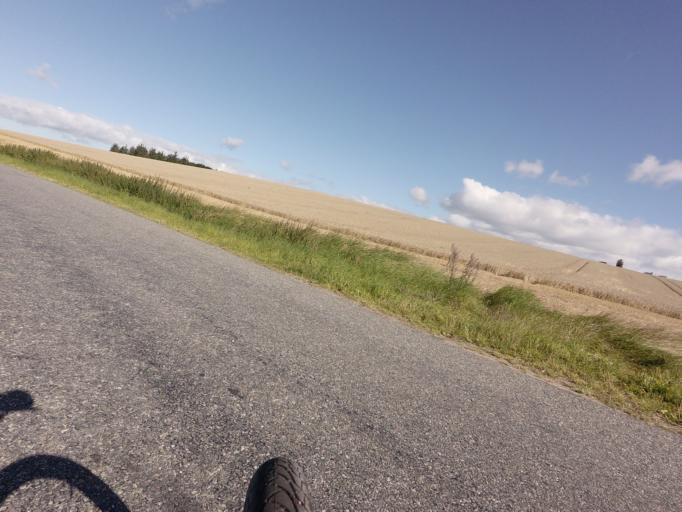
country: DK
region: Central Jutland
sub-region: Horsens Kommune
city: Horsens
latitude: 55.9595
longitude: 9.7705
